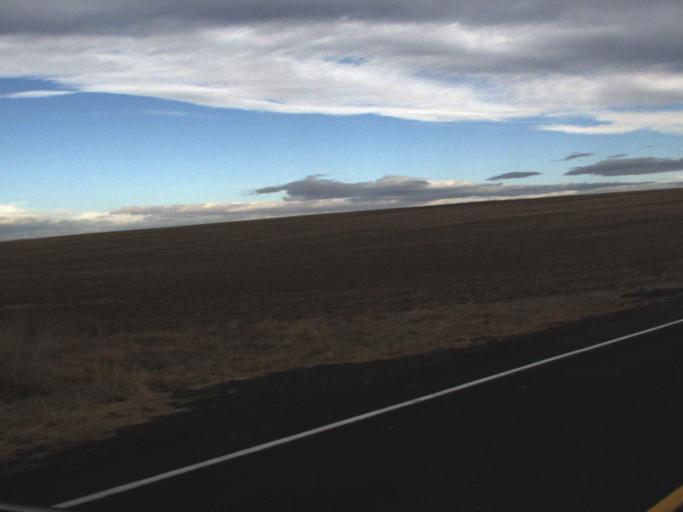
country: US
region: Washington
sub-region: Okanogan County
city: Coulee Dam
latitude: 47.7172
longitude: -118.7220
